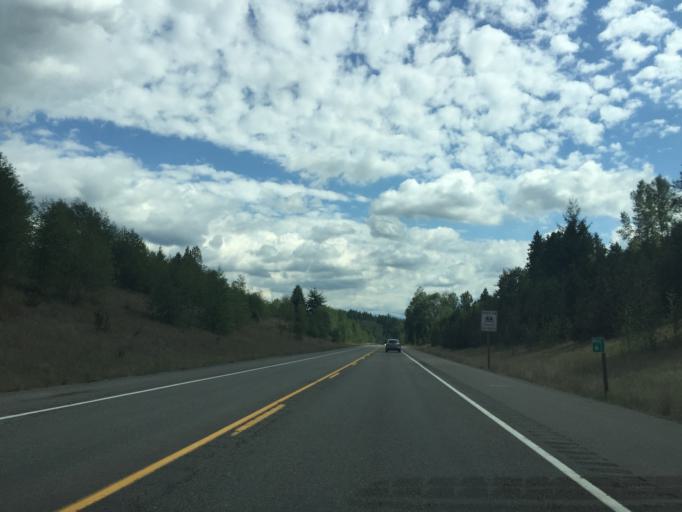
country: US
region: Washington
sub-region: Snohomish County
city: Fobes Hill
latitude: 47.9477
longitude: -122.0829
